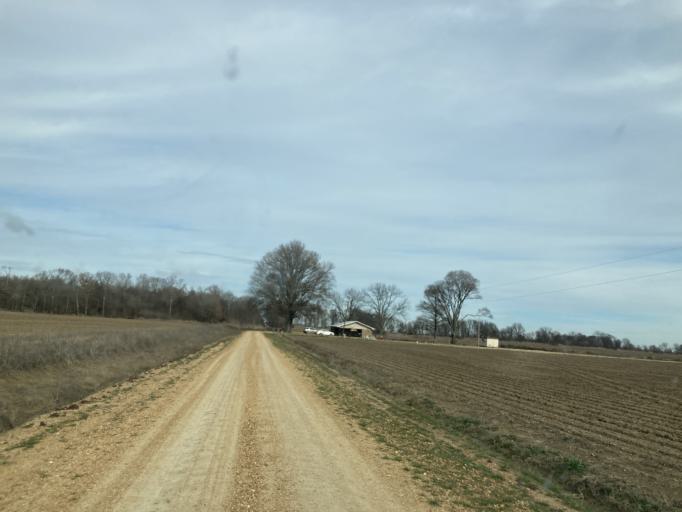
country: US
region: Mississippi
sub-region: Humphreys County
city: Belzoni
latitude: 33.0652
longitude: -90.6578
